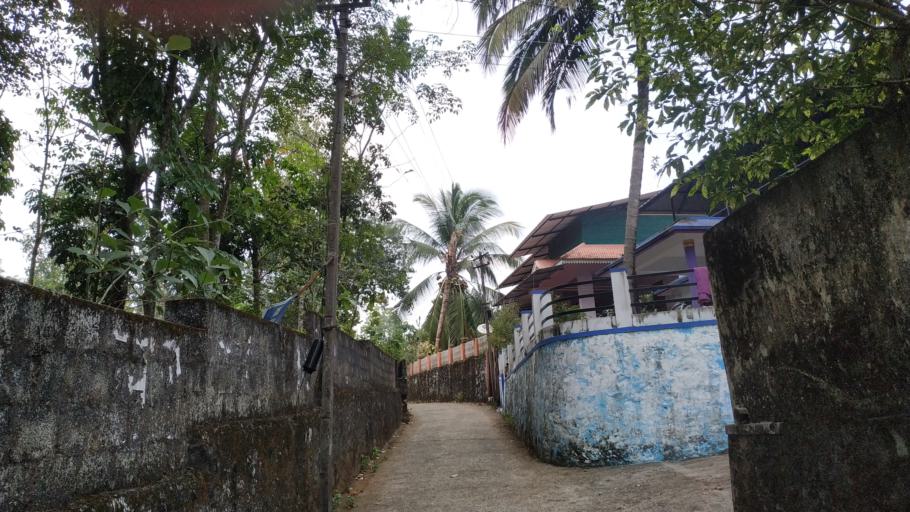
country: IN
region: Kerala
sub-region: Kottayam
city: Lalam
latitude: 9.8426
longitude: 76.7455
